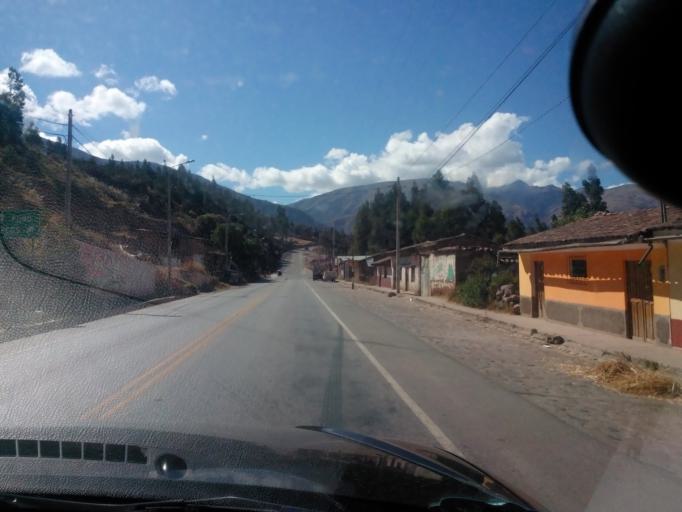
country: PE
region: Cusco
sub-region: Provincia de Quispicanchis
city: Huaro
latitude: -13.6856
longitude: -71.6317
